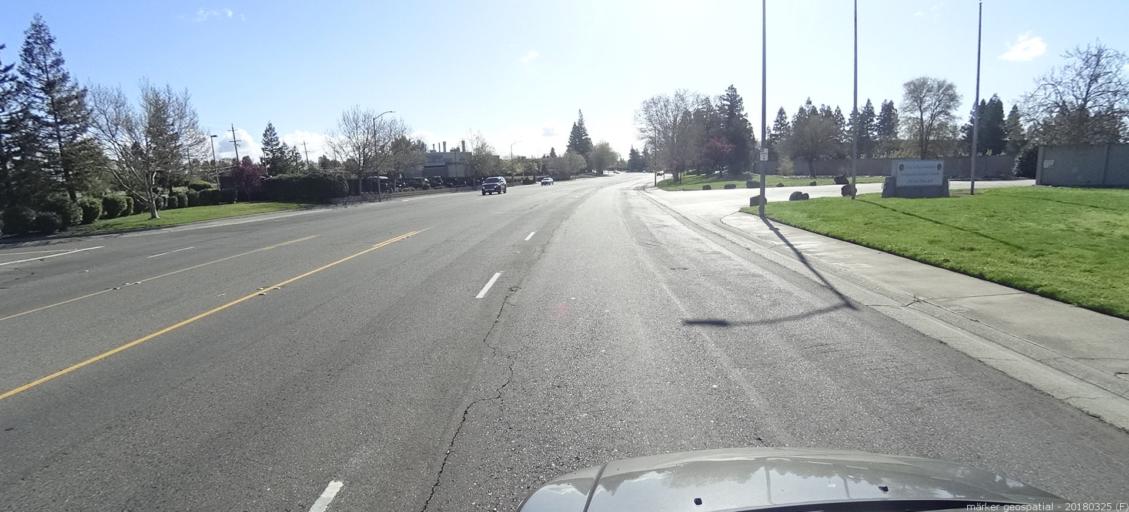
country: US
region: California
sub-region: Sacramento County
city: Rio Linda
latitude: 38.6562
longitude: -121.4825
